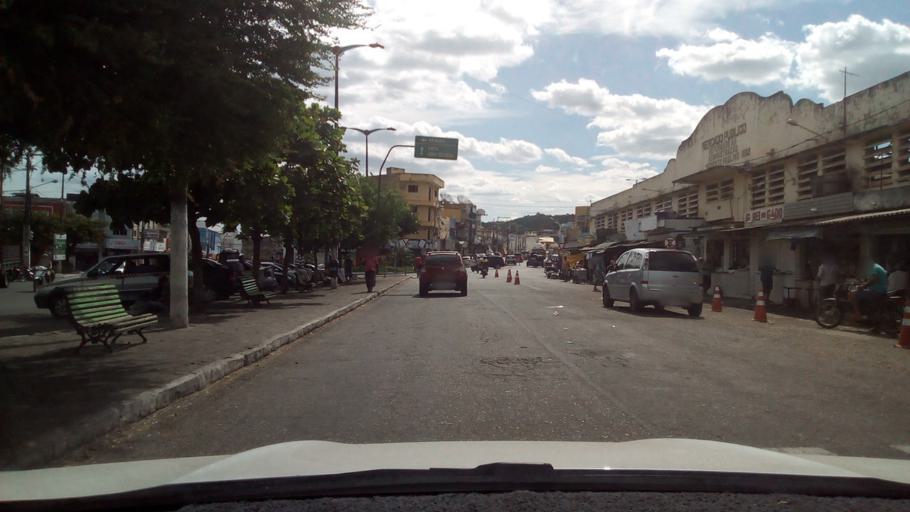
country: BR
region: Paraiba
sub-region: Guarabira
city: Guarabira
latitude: -6.8508
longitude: -35.4917
